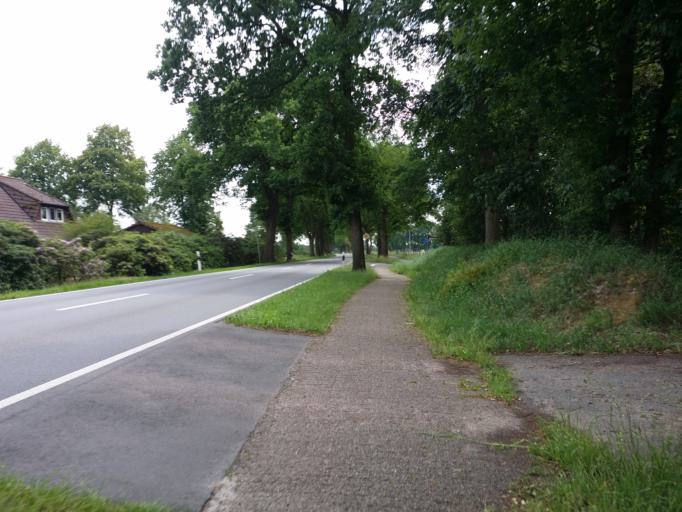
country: DE
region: Lower Saxony
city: Wiefelstede
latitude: 53.2737
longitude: 8.1108
